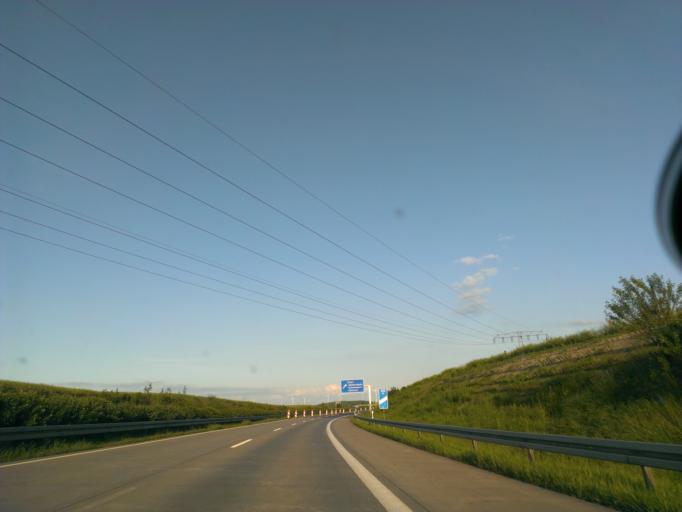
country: DE
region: Thuringia
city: Noda
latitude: 51.0396
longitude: 11.0313
